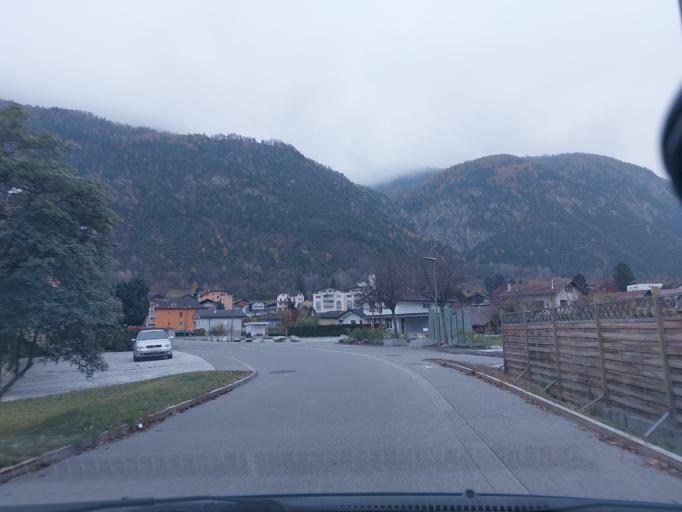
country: CH
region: Valais
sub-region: Sierre District
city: Grone
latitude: 46.2534
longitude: 7.4583
